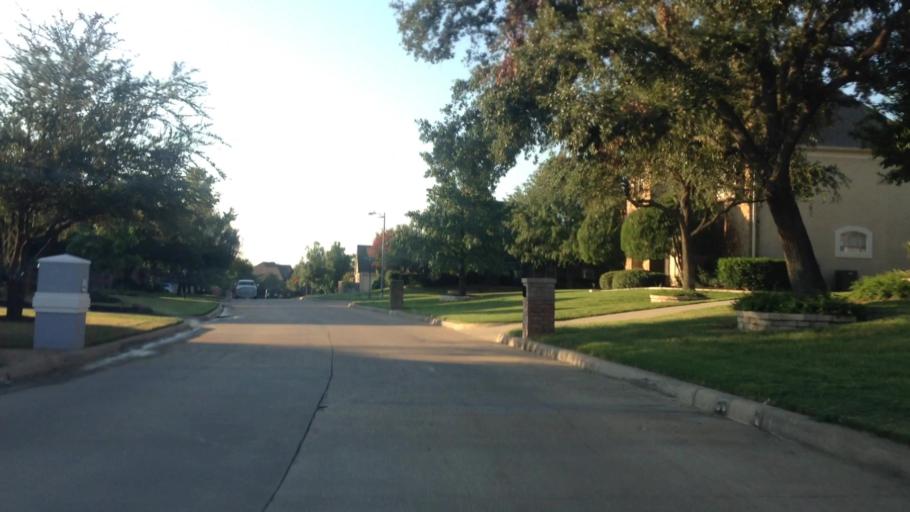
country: US
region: Texas
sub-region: Denton County
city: Trophy Club
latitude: 33.0031
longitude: -97.1688
